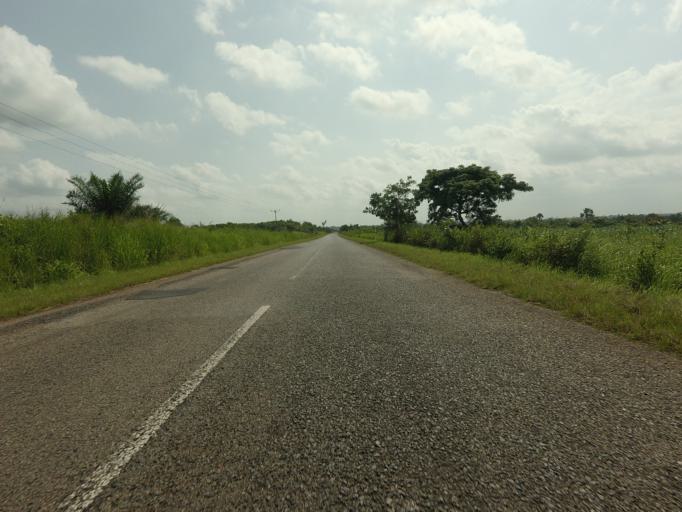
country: TG
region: Maritime
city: Tsevie
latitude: 6.3923
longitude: 0.8224
